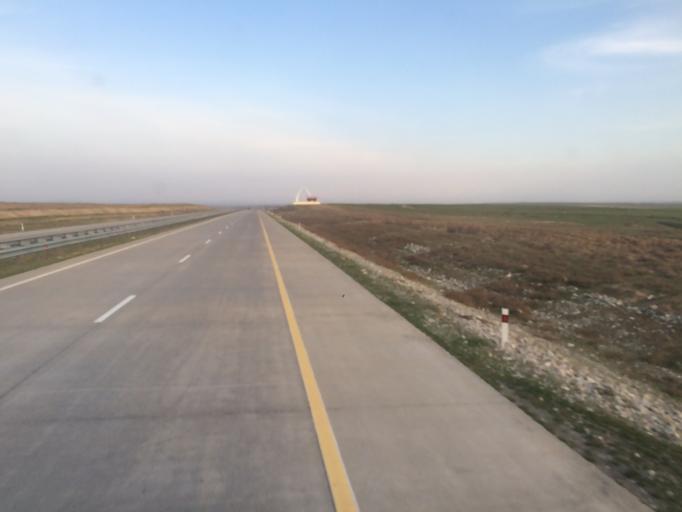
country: KZ
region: Ongtustik Qazaqstan
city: Shymkent
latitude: 42.4941
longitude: 69.4732
